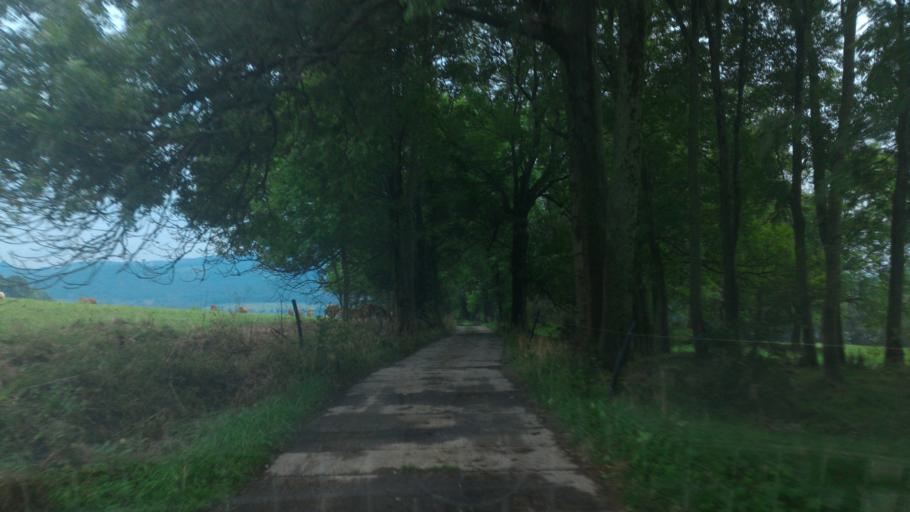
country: CZ
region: Ustecky
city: Dolni Podluzi
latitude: 50.8944
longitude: 14.5582
